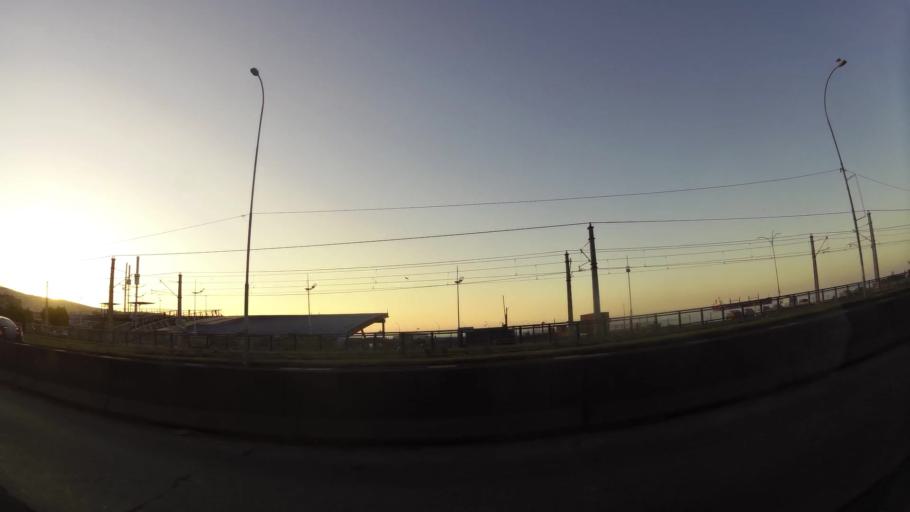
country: CL
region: Valparaiso
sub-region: Provincia de Valparaiso
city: Vina del Mar
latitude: -33.0312
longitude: -71.5885
